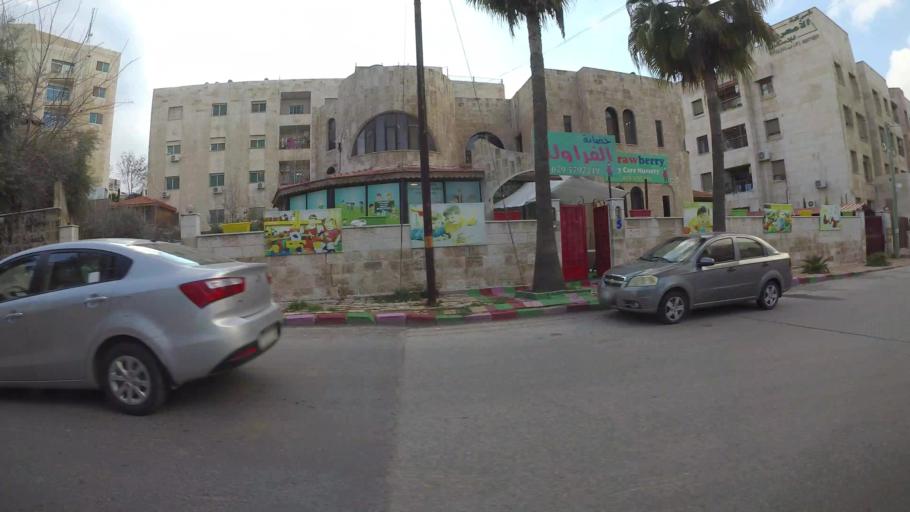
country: JO
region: Amman
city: Al Jubayhah
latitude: 31.9854
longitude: 35.8608
